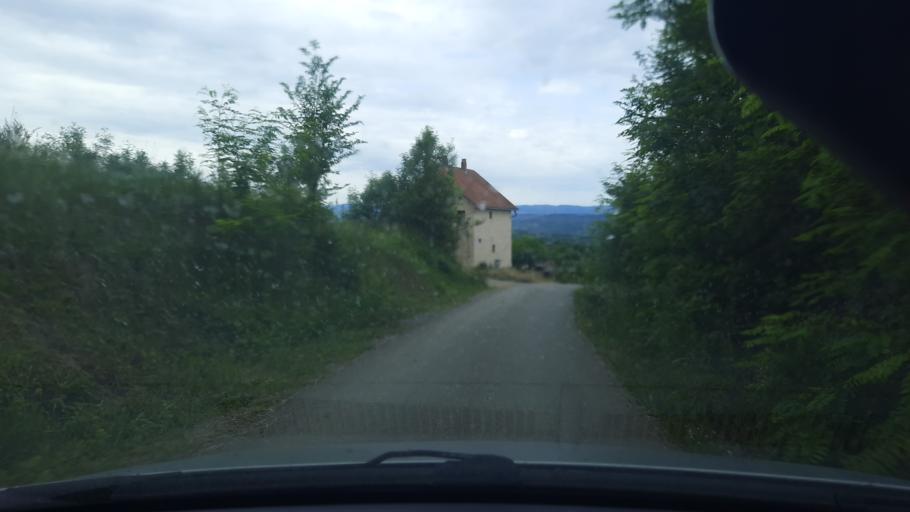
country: RS
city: Jarebice
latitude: 44.5056
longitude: 19.4766
